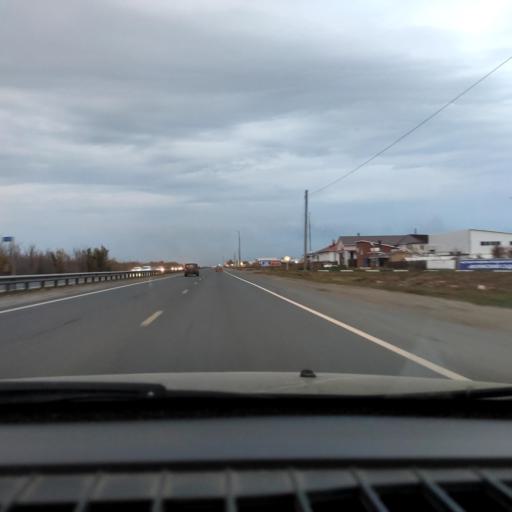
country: RU
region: Samara
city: Tol'yatti
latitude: 53.5627
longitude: 49.3643
